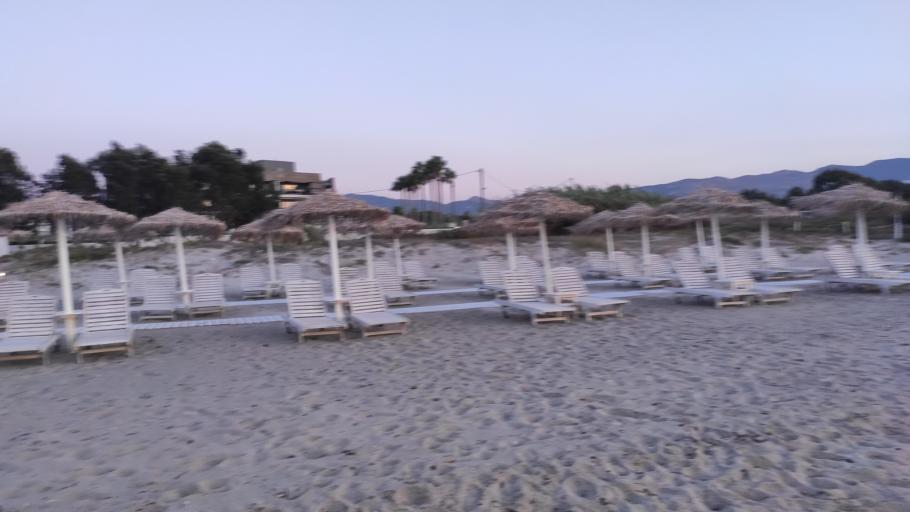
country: GR
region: South Aegean
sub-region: Nomos Dodekanisou
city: Kos
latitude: 36.9152
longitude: 27.2767
